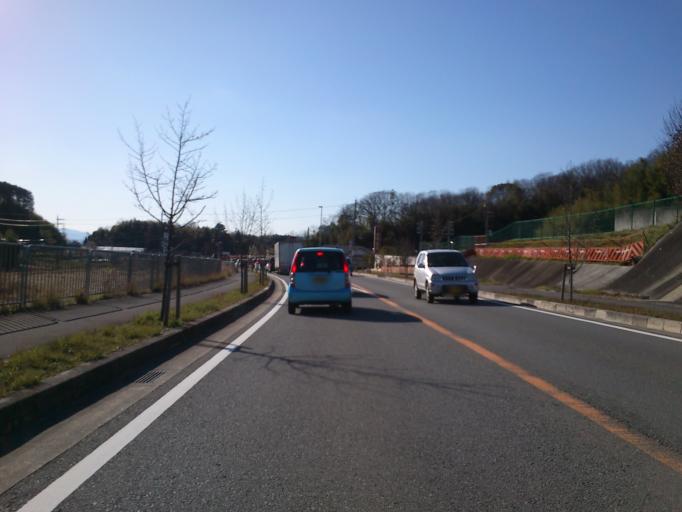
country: JP
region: Kyoto
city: Tanabe
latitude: 34.8134
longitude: 135.7330
